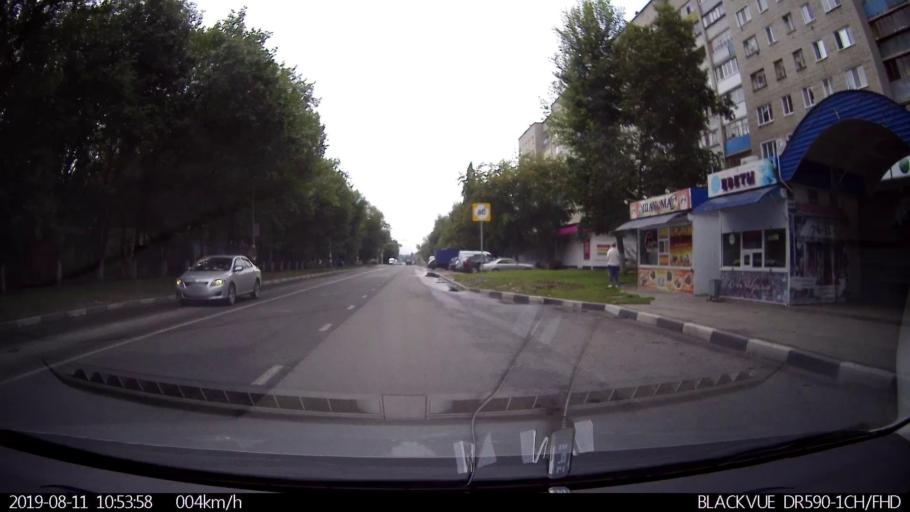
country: RU
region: Ulyanovsk
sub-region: Ulyanovskiy Rayon
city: Ulyanovsk
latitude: 54.2589
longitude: 48.3343
